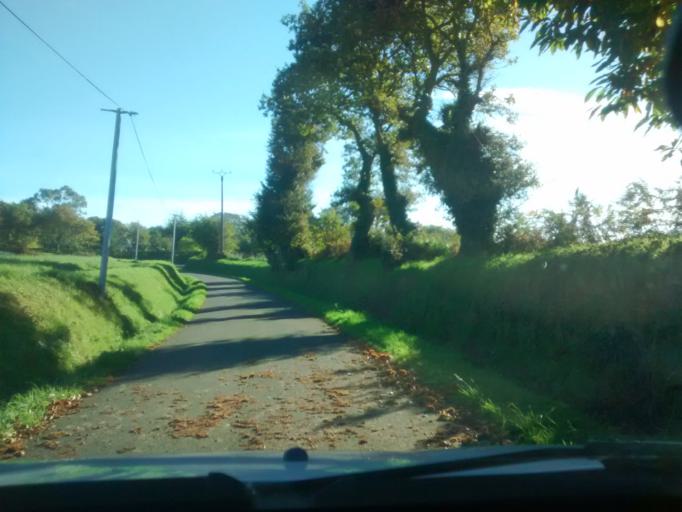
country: FR
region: Brittany
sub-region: Departement des Cotes-d'Armor
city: Saint-Quay-Perros
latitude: 48.7804
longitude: -3.4341
